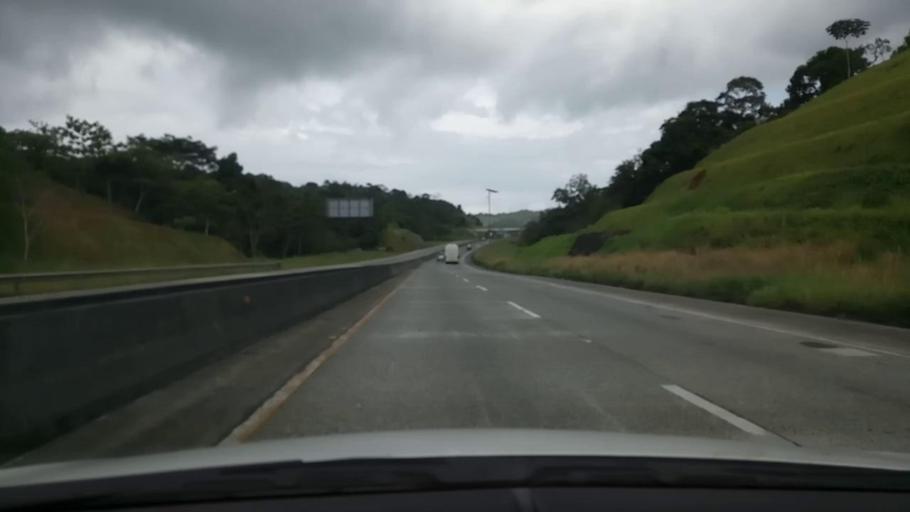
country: PA
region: Colon
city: Gatun
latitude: 9.2822
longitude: -79.7681
